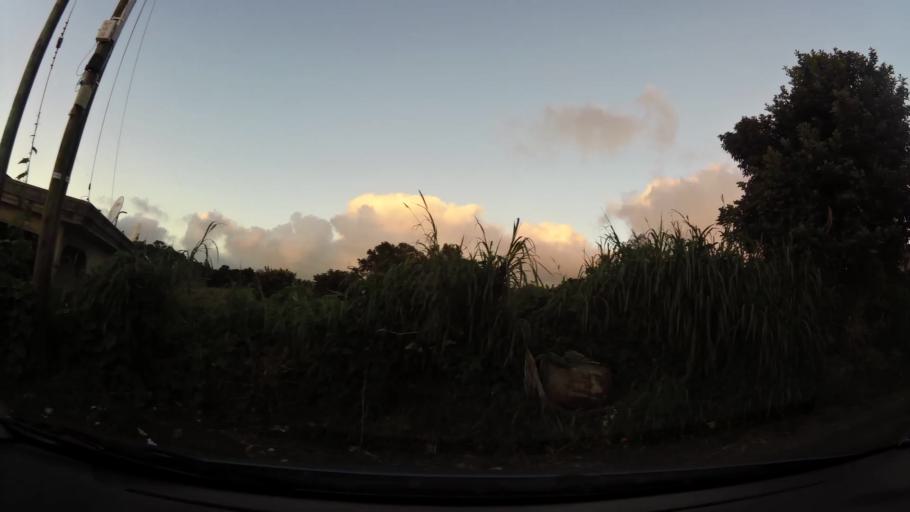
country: MU
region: Plaines Wilhems
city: Curepipe
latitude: -20.2979
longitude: 57.5244
